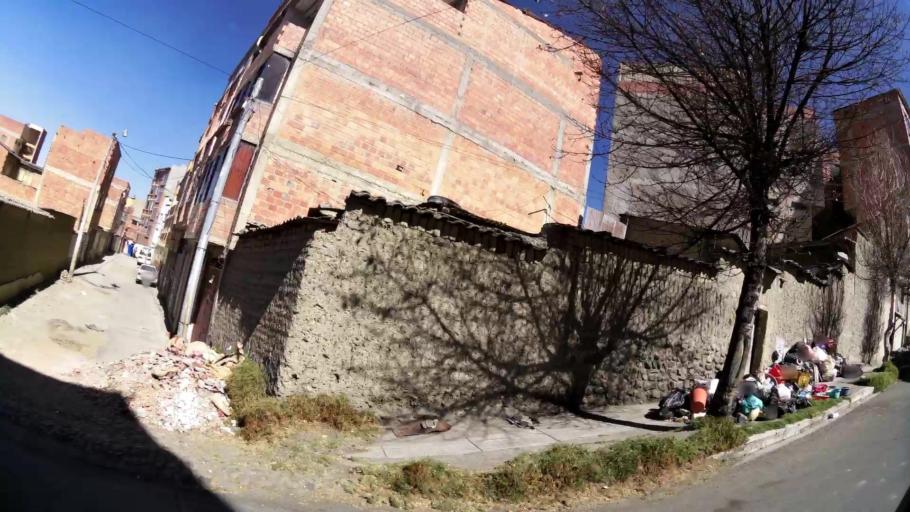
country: BO
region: La Paz
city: La Paz
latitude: -16.4920
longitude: -68.1612
